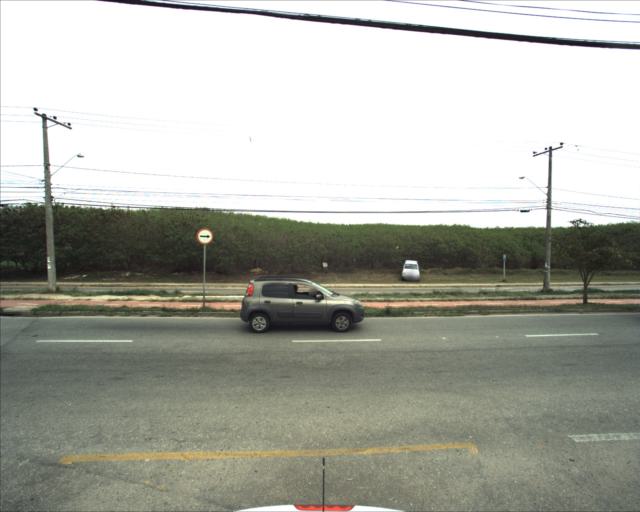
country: BR
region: Sao Paulo
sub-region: Sorocaba
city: Sorocaba
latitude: -23.4978
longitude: -47.5283
